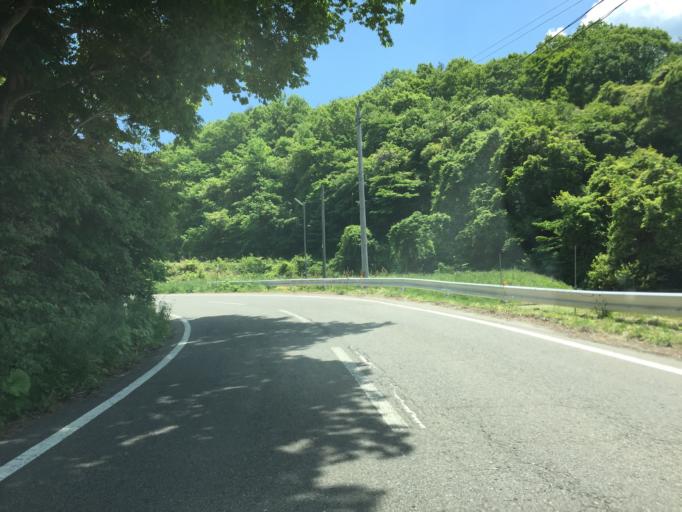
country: JP
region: Fukushima
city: Funehikimachi-funehiki
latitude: 37.5138
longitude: 140.6878
